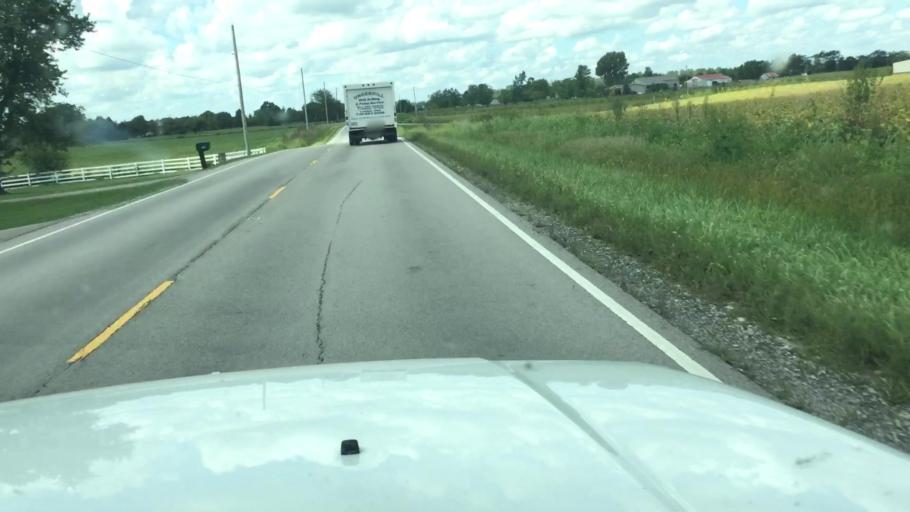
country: US
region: Ohio
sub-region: Madison County
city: London
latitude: 39.8283
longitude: -83.3658
